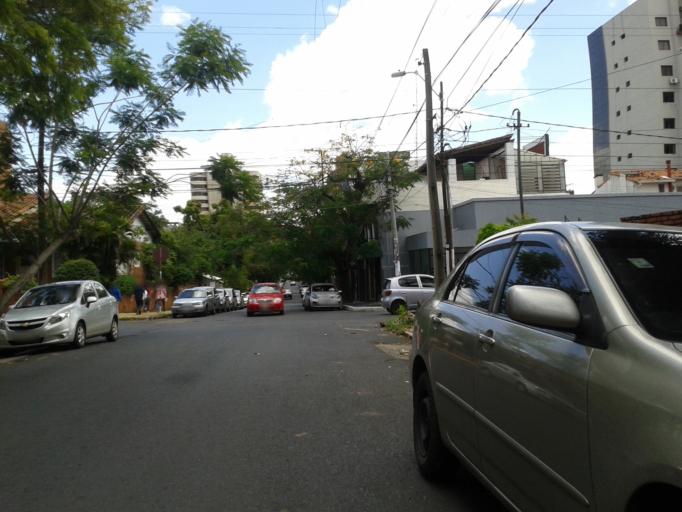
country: PY
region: Asuncion
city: Asuncion
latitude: -25.2939
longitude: -57.6161
